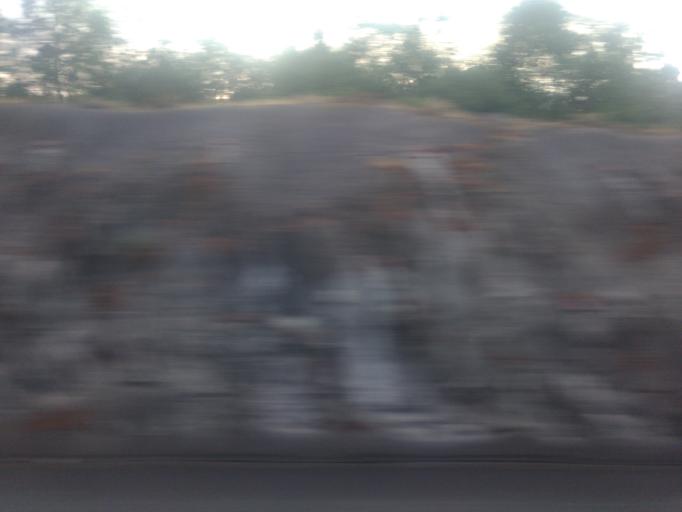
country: MX
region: Veracruz
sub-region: Acajete
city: La Joya
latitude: 19.6247
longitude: -97.0277
